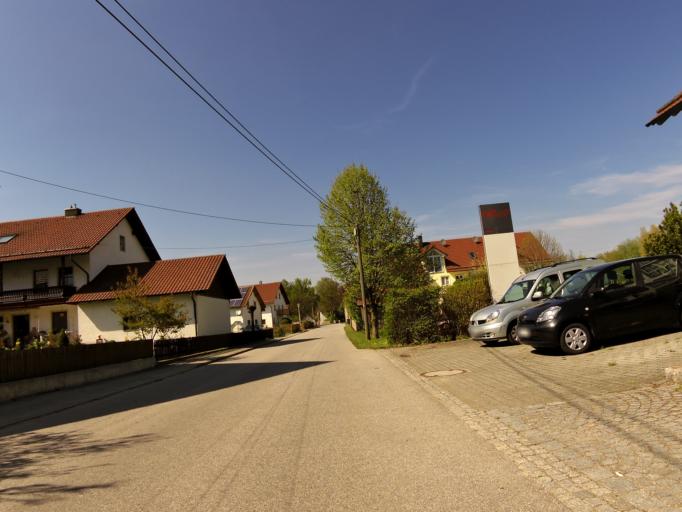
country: DE
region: Bavaria
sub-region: Upper Bavaria
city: Wartenberg
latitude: 48.3954
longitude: 11.9656
